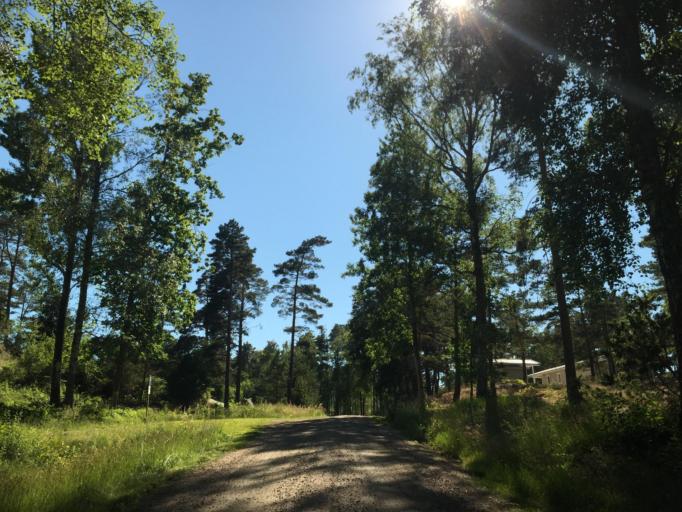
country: SE
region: Vaestra Goetaland
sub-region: Stromstads Kommun
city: Stroemstad
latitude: 58.8615
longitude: 11.2242
